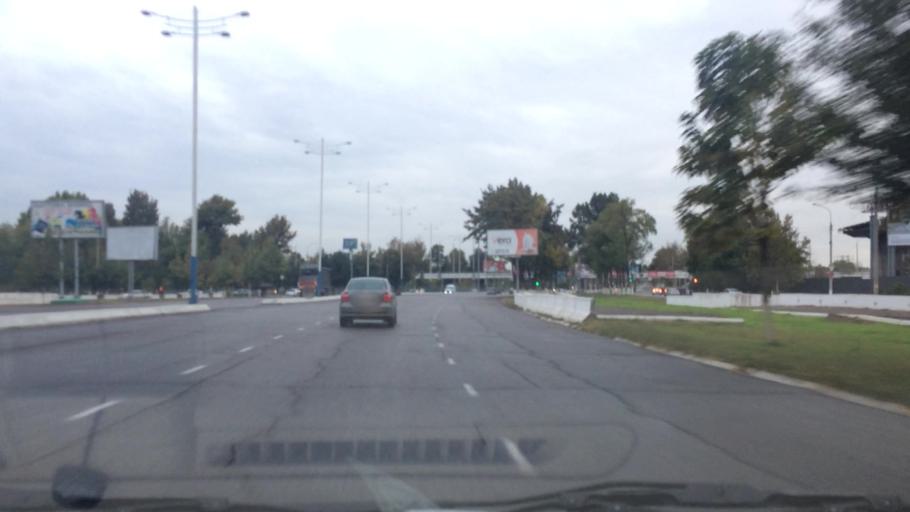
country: UZ
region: Toshkent Shahri
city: Tashkent
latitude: 41.2582
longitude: 69.1952
